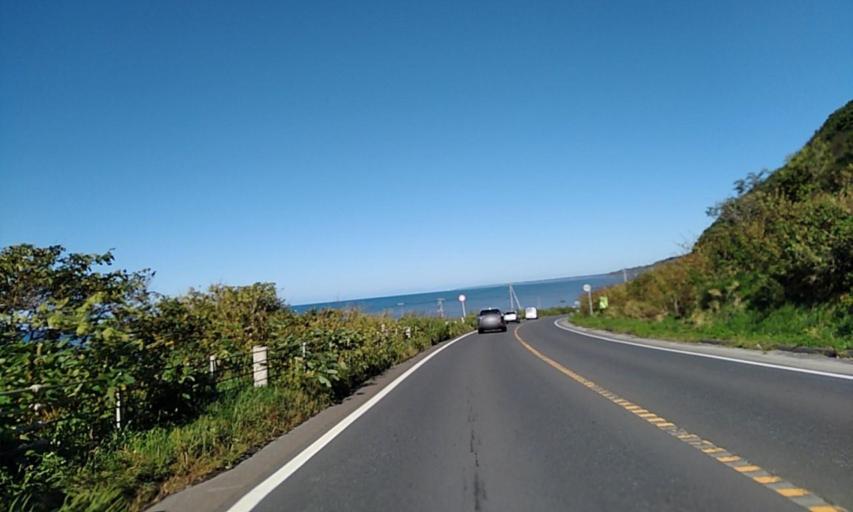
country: JP
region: Hokkaido
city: Shizunai-furukawacho
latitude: 42.3844
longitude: 142.2734
